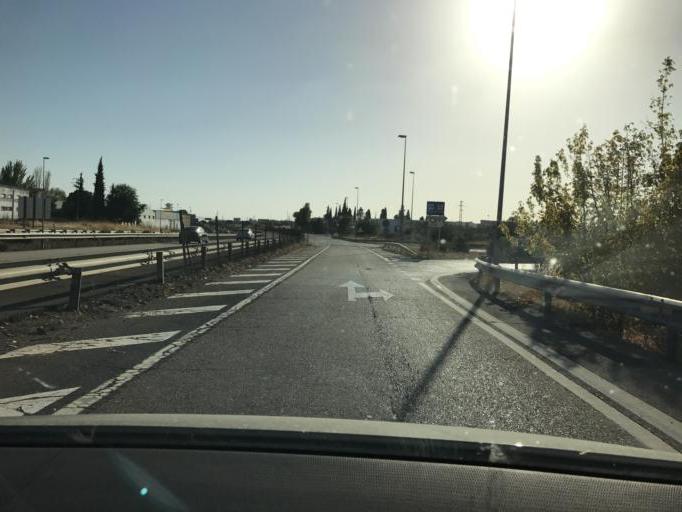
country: ES
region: Andalusia
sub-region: Provincia de Jaen
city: La Carolina
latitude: 38.2816
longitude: -3.5952
